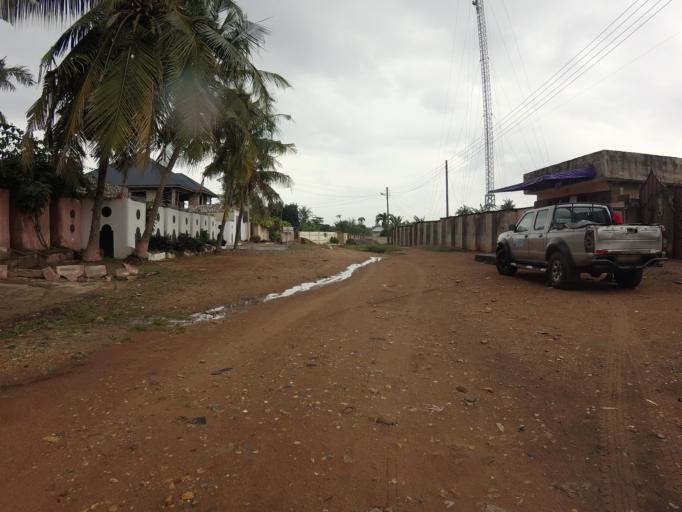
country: GH
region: Greater Accra
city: Dome
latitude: 5.6317
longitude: -0.2303
